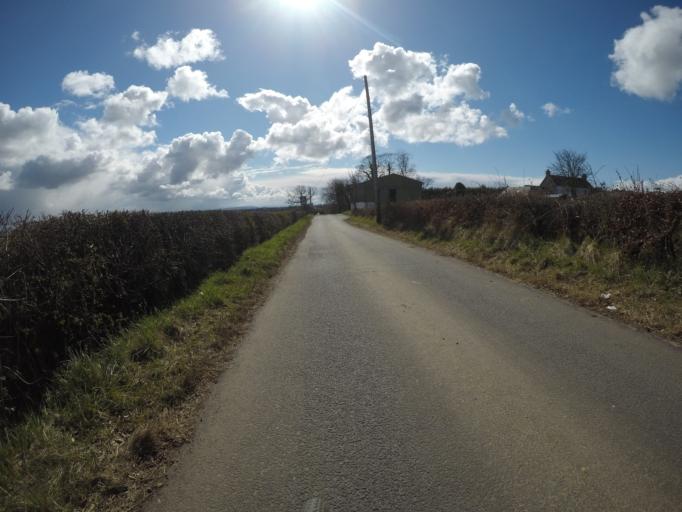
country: GB
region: Scotland
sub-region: North Ayrshire
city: Kilwinning
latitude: 55.6717
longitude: -4.7217
